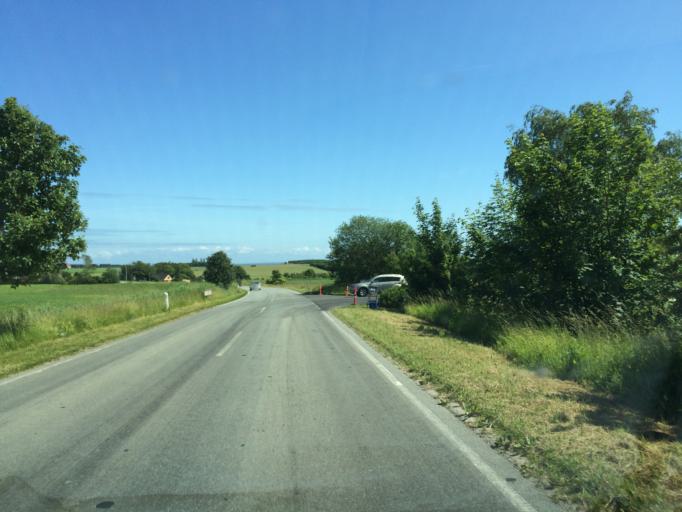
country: DK
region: Central Jutland
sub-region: Samso Kommune
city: Tranebjerg
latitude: 55.8131
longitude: 10.6165
